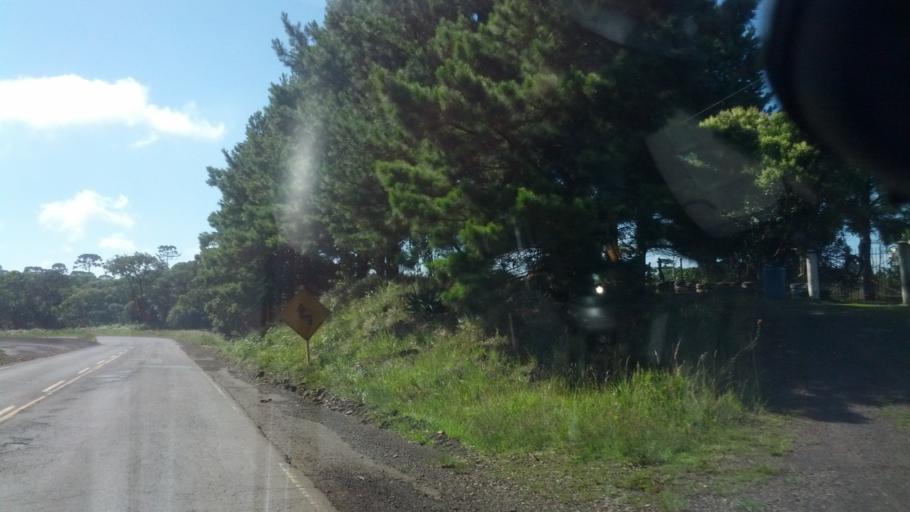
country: BR
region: Santa Catarina
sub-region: Lages
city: Lages
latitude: -27.9492
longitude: -50.5021
